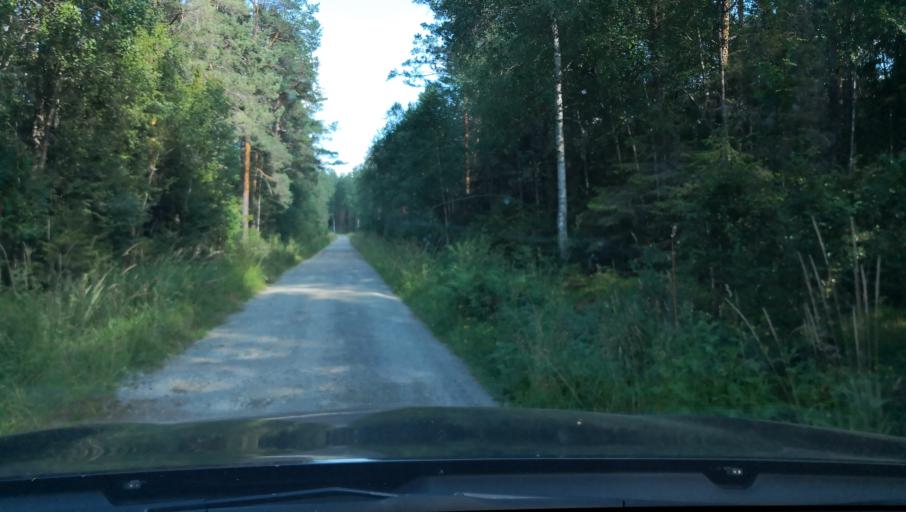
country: SE
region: Vaestmanland
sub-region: Vasteras
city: Skultuna
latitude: 59.7242
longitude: 16.3454
